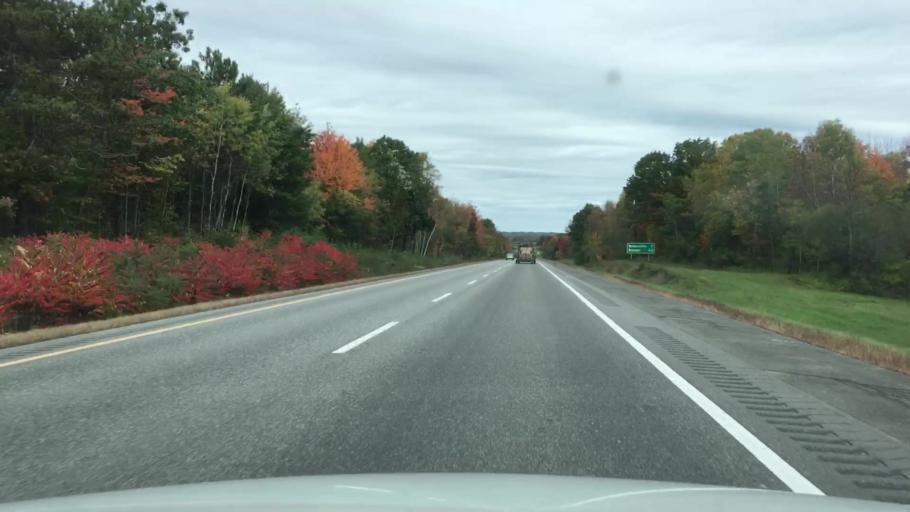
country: US
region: Maine
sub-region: Kennebec County
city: Vassalboro
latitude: 44.4638
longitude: -69.7114
